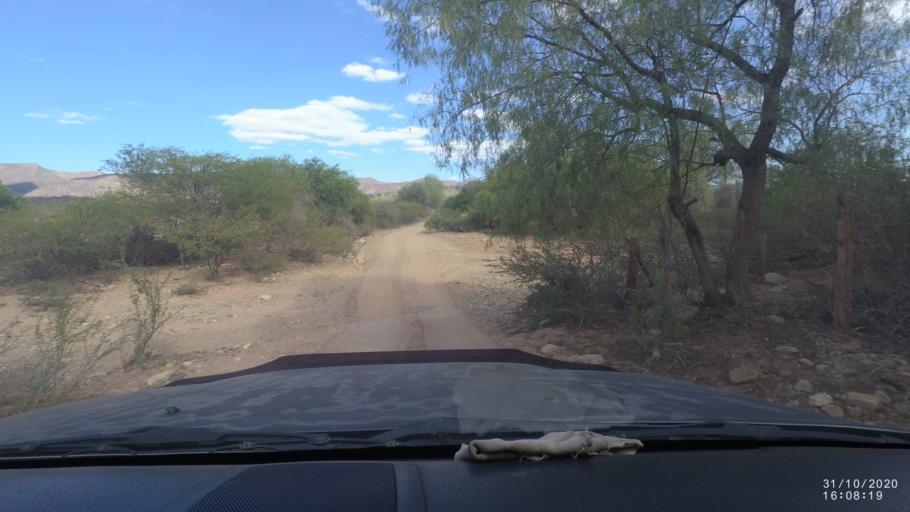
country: BO
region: Chuquisaca
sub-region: Provincia Zudanez
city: Mojocoya
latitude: -18.3842
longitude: -64.6412
